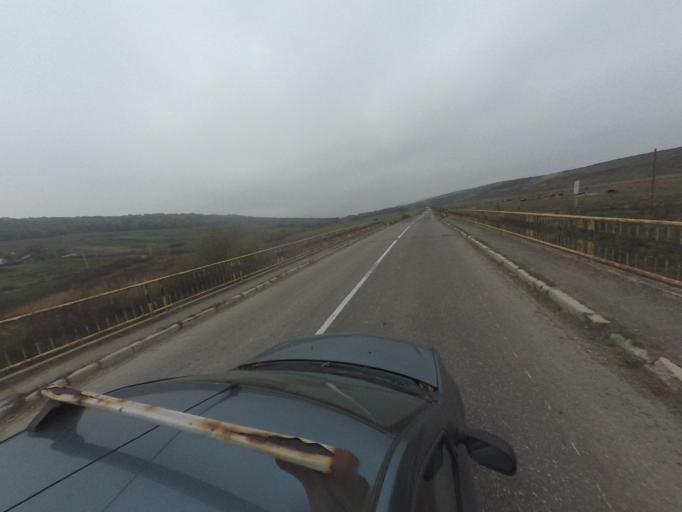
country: RO
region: Vaslui
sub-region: Comuna Bacesti
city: Bacesti
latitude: 46.8377
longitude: 27.2274
